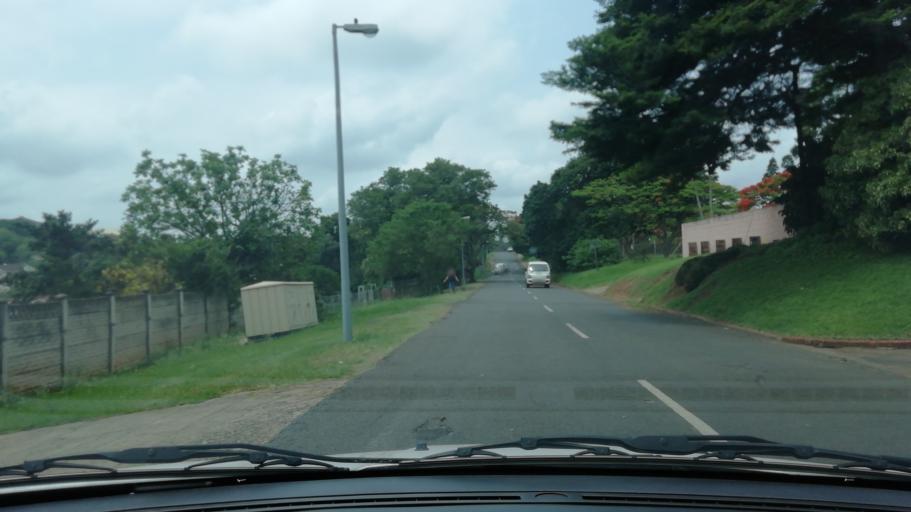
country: ZA
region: KwaZulu-Natal
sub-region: uThungulu District Municipality
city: Empangeni
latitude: -28.7506
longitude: 31.8904
